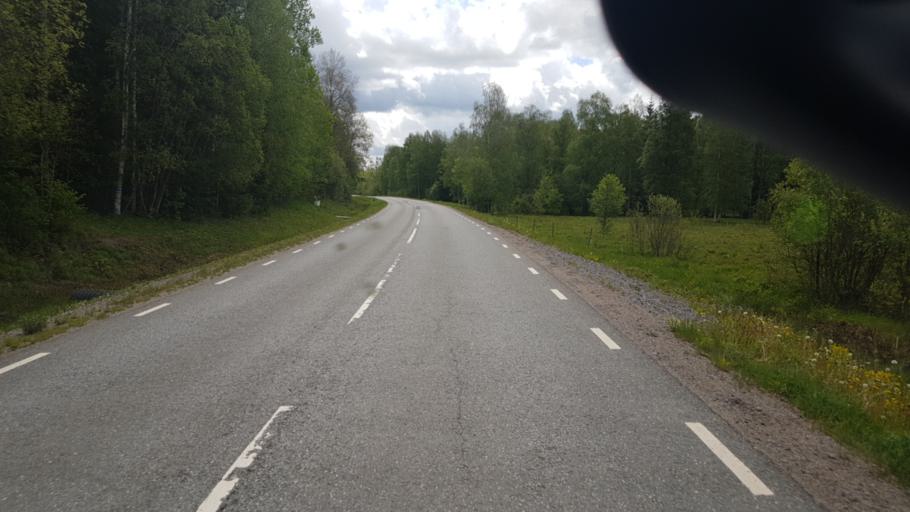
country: SE
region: Vaermland
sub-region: Eda Kommun
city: Amotfors
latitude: 59.6915
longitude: 12.0924
